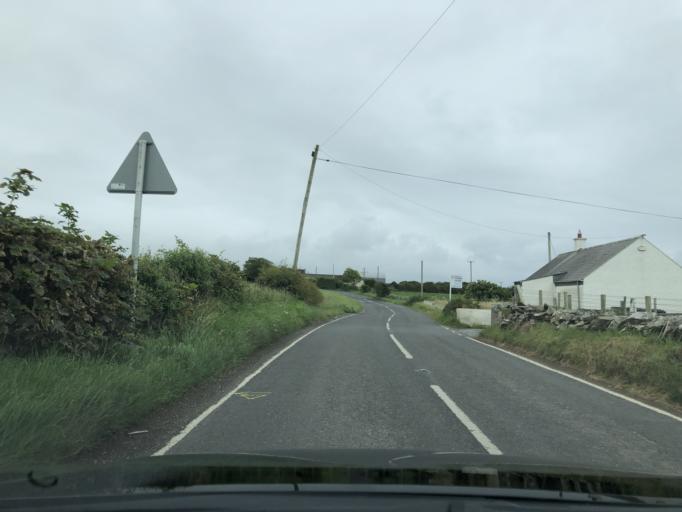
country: GB
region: Northern Ireland
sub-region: Down District
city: Dundrum
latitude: 54.2535
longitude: -5.7664
